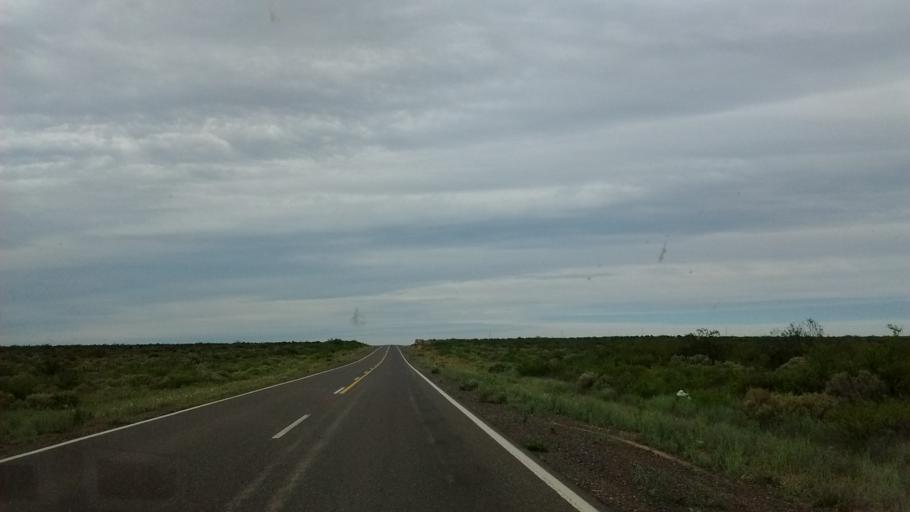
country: AR
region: Rio Negro
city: Catriel
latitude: -38.0595
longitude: -67.9212
